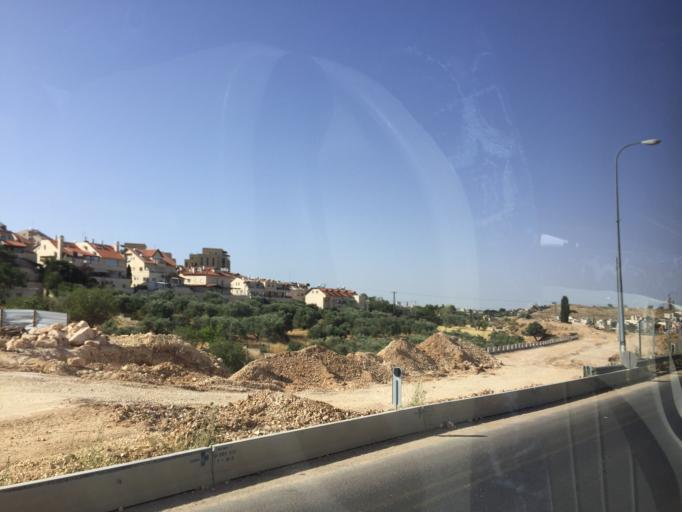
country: PS
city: Khallat Hamamah
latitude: 31.7279
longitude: 35.1993
